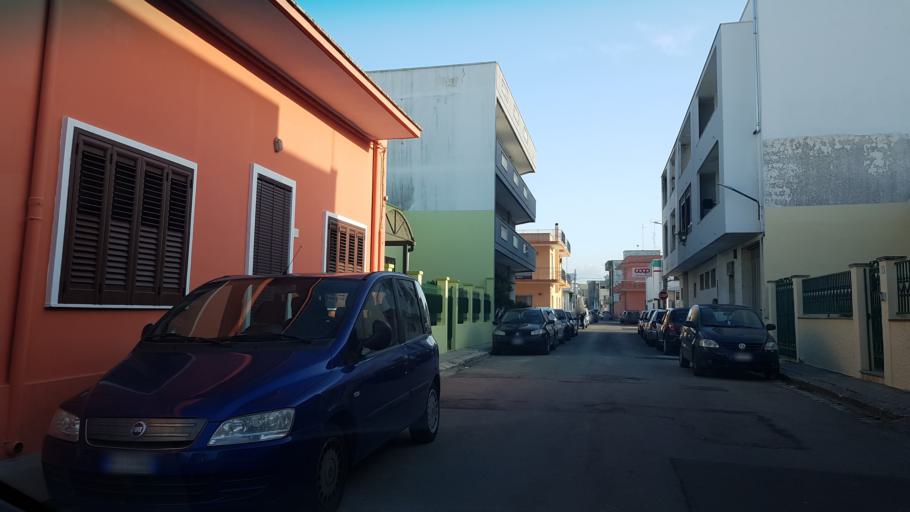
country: IT
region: Apulia
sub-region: Provincia di Lecce
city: Trepuzzi
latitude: 40.4088
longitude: 18.0721
